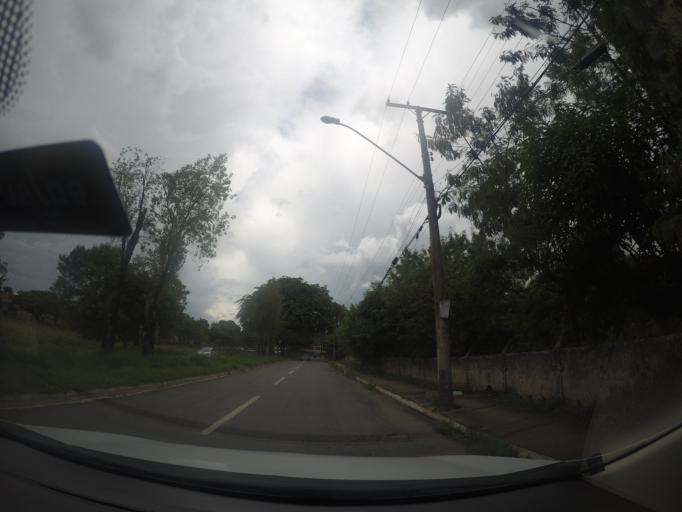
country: BR
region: Goias
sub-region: Goiania
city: Goiania
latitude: -16.6472
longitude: -49.2393
